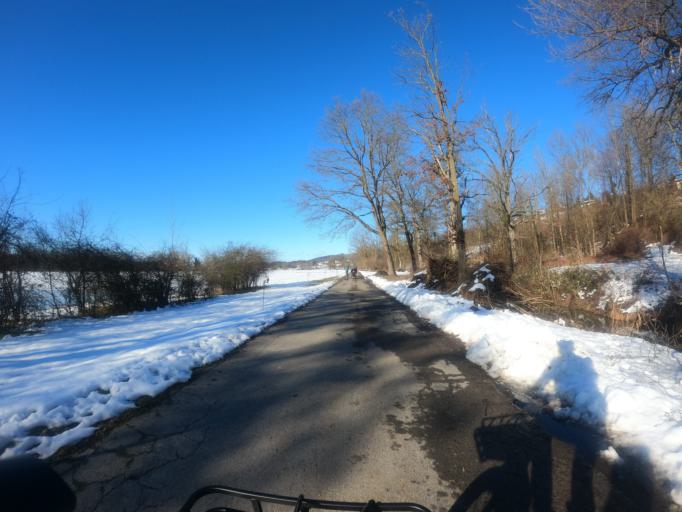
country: CH
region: Aargau
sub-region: Bezirk Bremgarten
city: Oberlunkhofen
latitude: 47.3120
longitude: 8.3853
